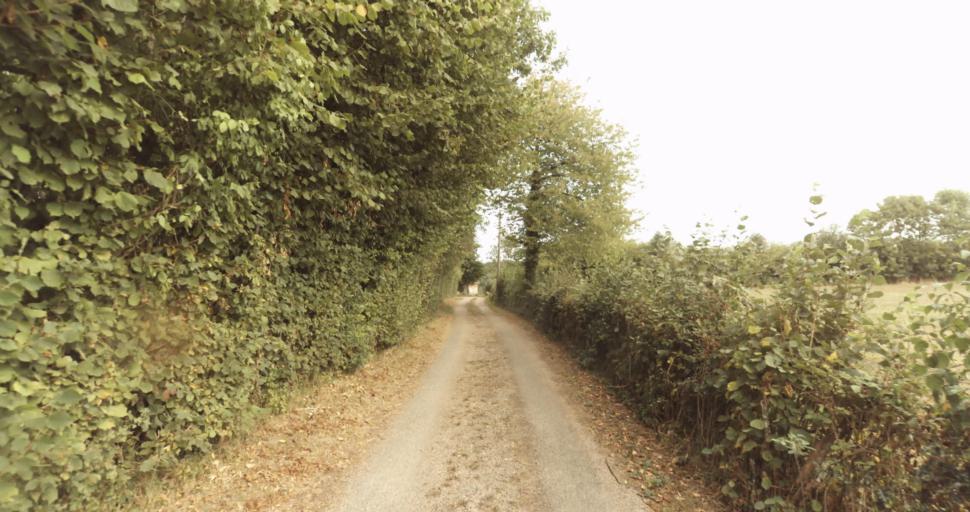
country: FR
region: Lower Normandy
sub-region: Departement de l'Orne
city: Vimoutiers
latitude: 48.9249
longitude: 0.2296
